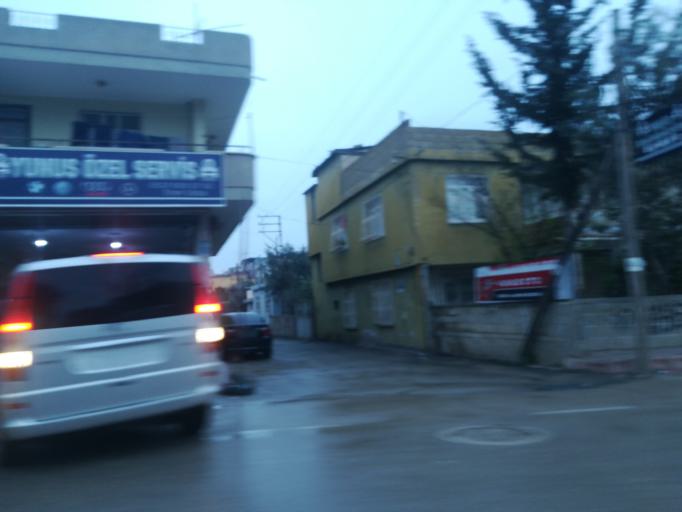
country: TR
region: Adana
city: Seyhan
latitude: 37.0151
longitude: 35.2759
